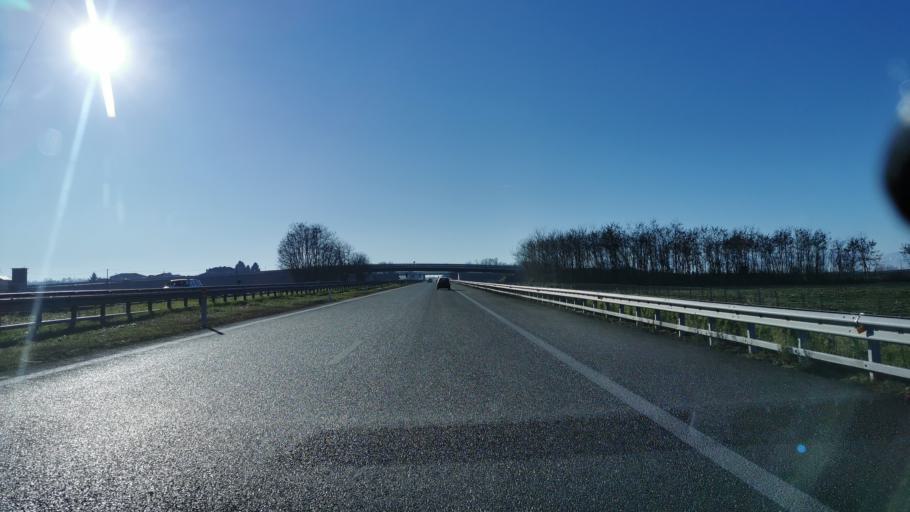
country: IT
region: Piedmont
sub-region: Provincia di Cuneo
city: Caramagna Piemonte
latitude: 44.8206
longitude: 7.7503
